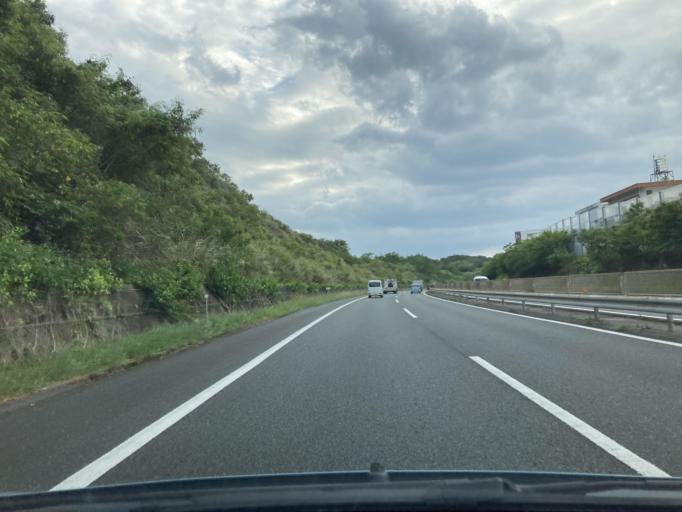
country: JP
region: Okinawa
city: Ginowan
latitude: 26.2519
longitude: 127.7610
